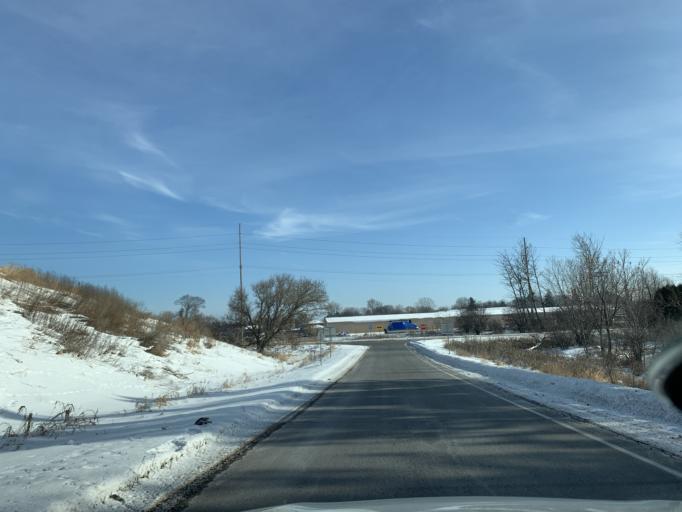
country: US
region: Minnesota
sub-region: Washington County
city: Forest Lake
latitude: 45.2885
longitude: -92.9871
